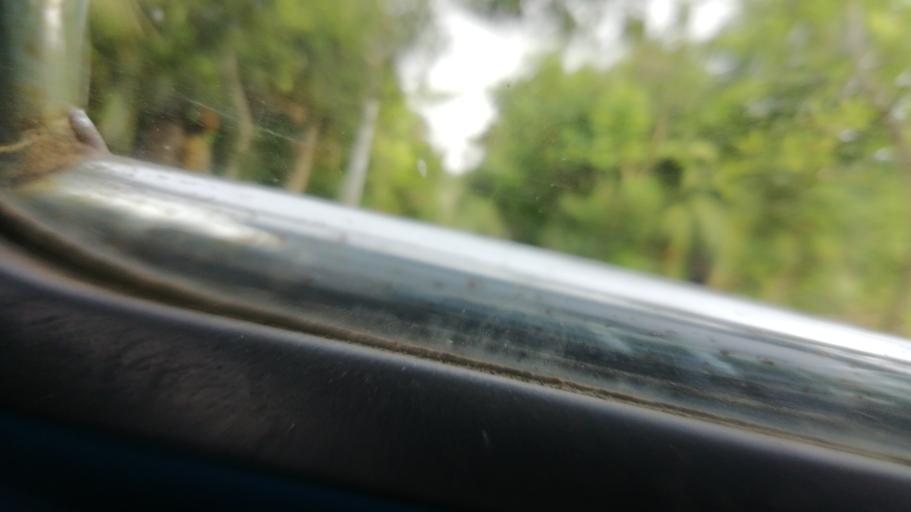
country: BD
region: Khulna
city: Kesabpur
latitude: 23.0253
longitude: 89.2583
